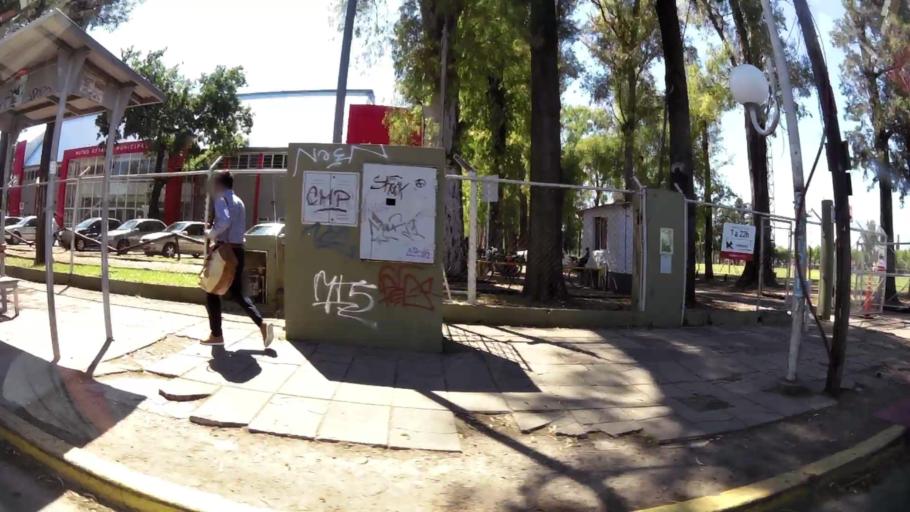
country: AR
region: Buenos Aires
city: Ituzaingo
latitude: -34.6596
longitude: -58.6608
